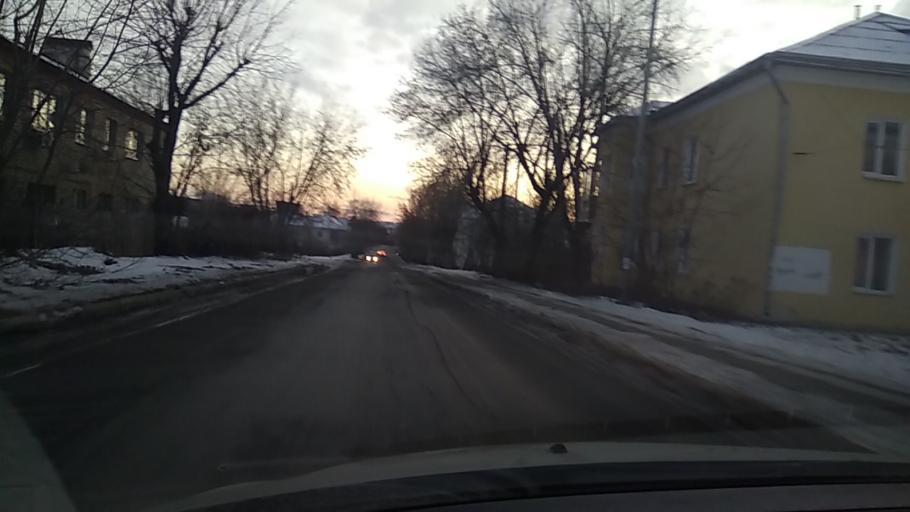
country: RU
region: Sverdlovsk
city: Istok
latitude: 56.7610
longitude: 60.7117
